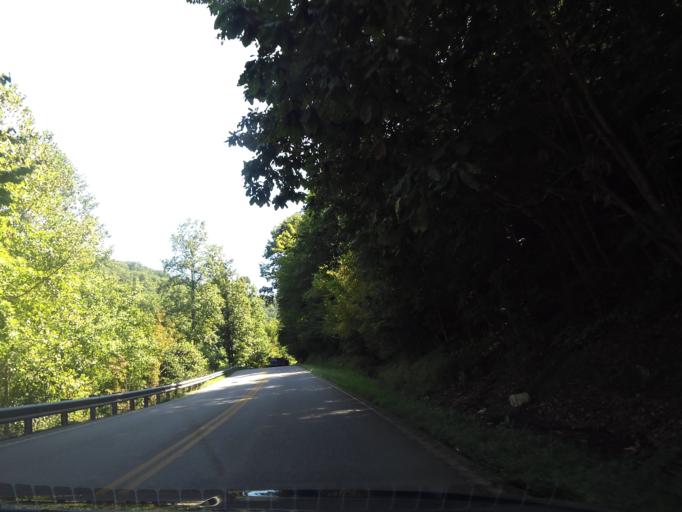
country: US
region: Kentucky
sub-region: Leslie County
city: Hyden
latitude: 37.1622
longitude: -83.5143
